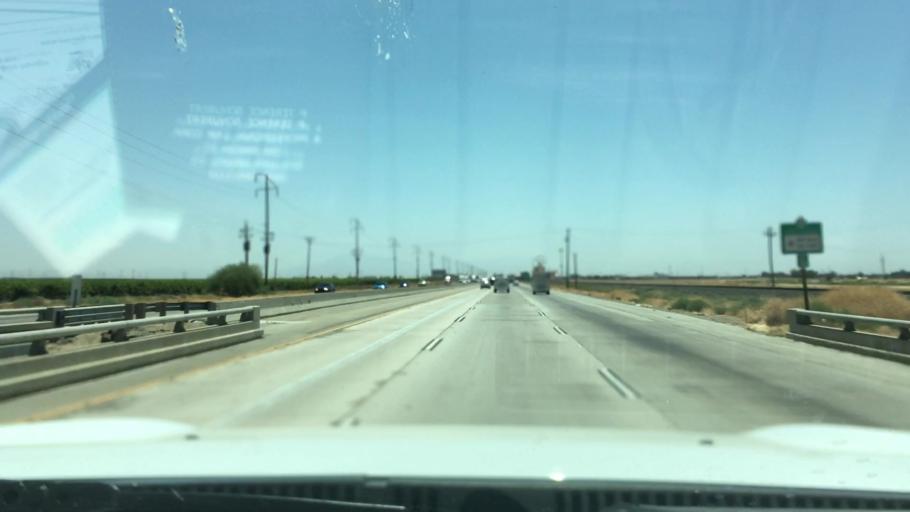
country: US
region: California
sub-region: Kern County
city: Greenacres
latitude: 35.4591
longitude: -119.1107
